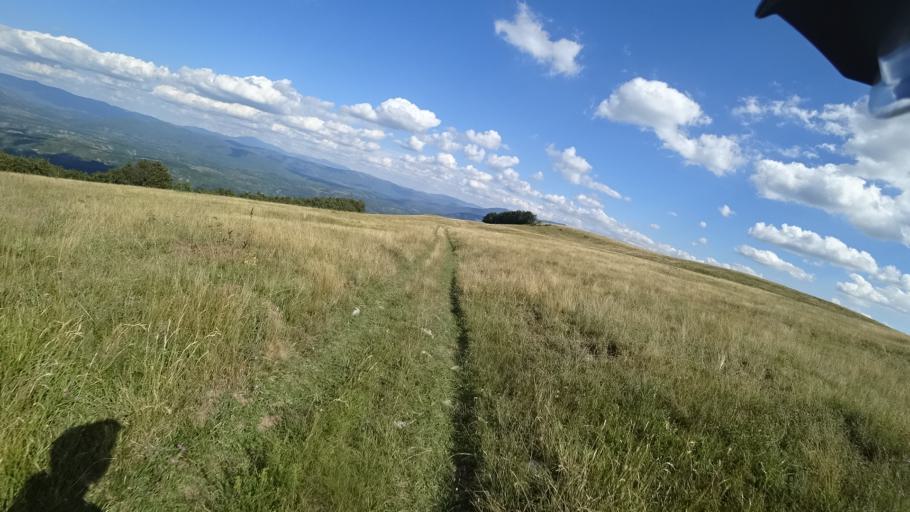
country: HR
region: Zadarska
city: Gracac
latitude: 44.3696
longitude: 16.0719
